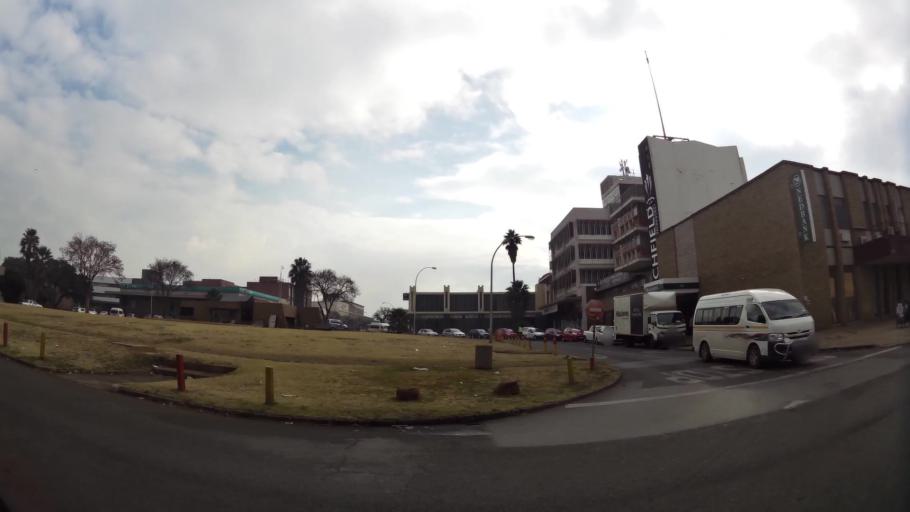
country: ZA
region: Gauteng
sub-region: Sedibeng District Municipality
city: Vanderbijlpark
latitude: -26.7005
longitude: 27.8358
